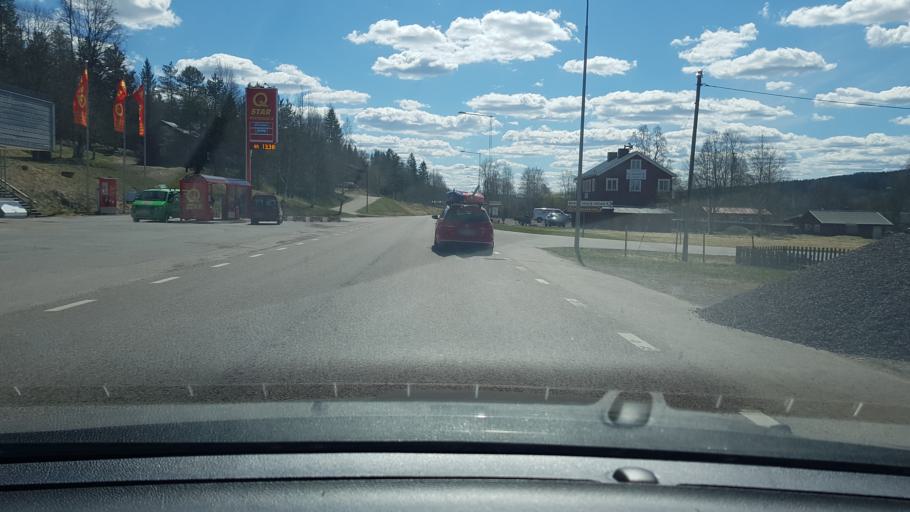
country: SE
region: Dalarna
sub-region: Malung-Saelens kommun
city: Malung
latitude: 61.1619
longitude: 13.2625
